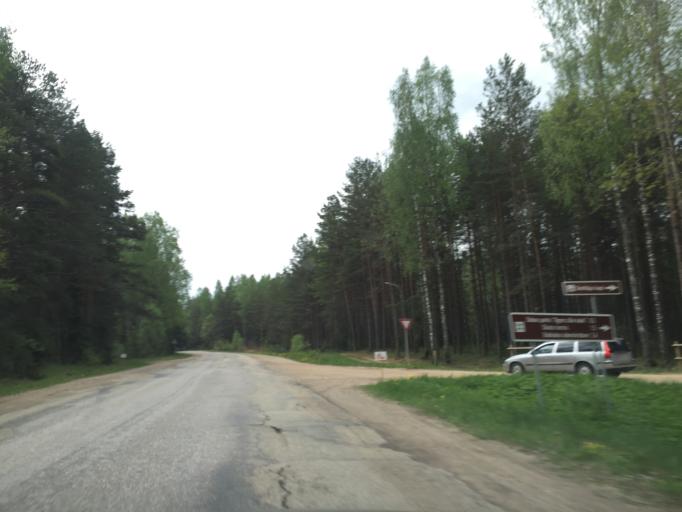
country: LV
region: Ogre
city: Ogre
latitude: 56.8378
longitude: 24.5776
